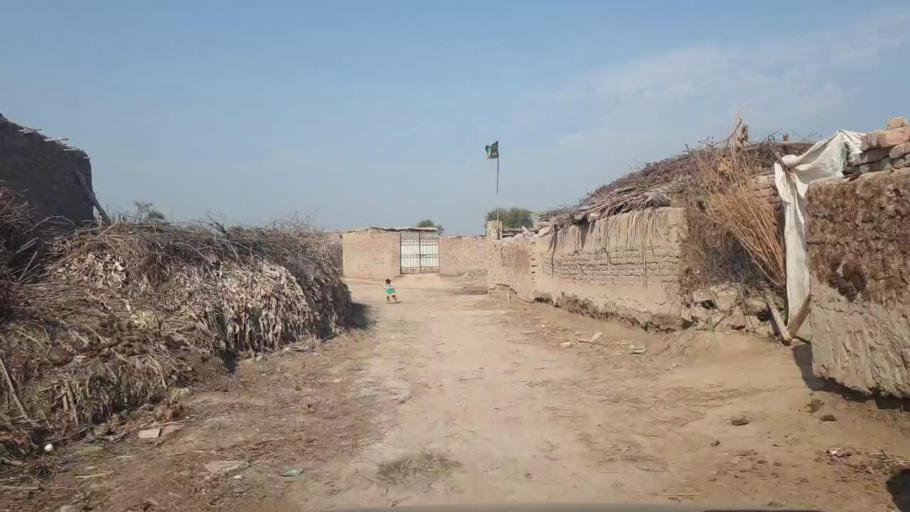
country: PK
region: Sindh
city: Tando Adam
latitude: 25.7467
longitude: 68.5888
